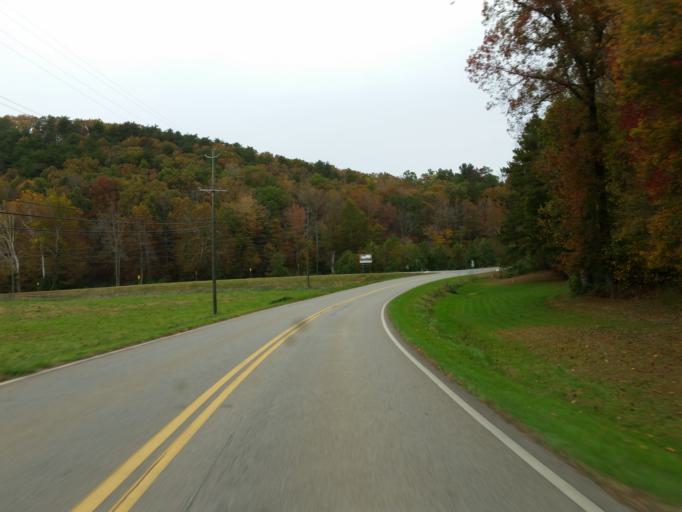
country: US
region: Georgia
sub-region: Pickens County
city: Jasper
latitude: 34.5095
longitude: -84.4422
